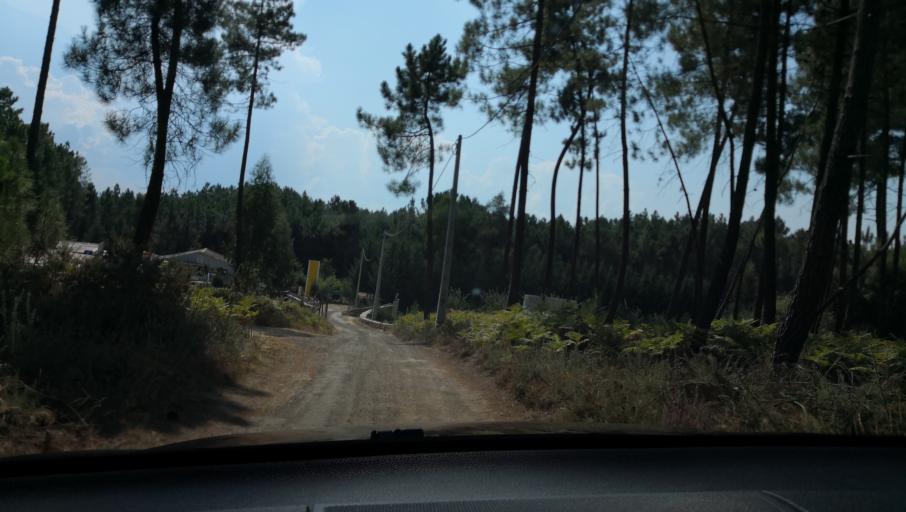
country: PT
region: Vila Real
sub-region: Sabrosa
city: Vilela
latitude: 41.2632
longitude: -7.6278
